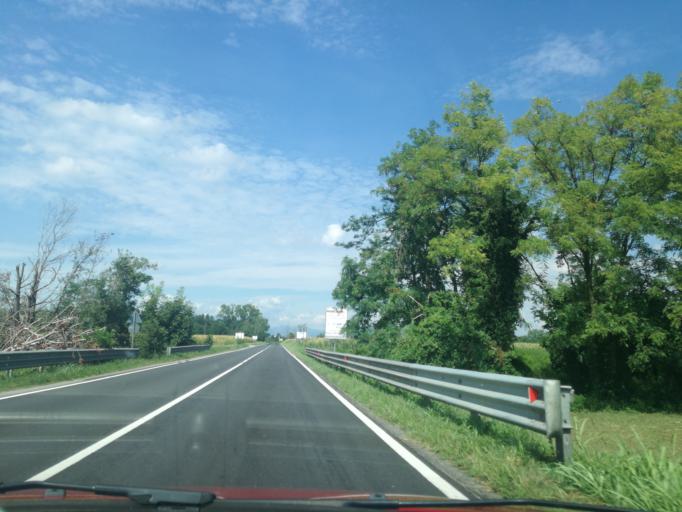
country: IT
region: Lombardy
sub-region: Citta metropolitana di Milano
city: Bellinzago Lombardo
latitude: 45.5502
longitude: 9.4560
